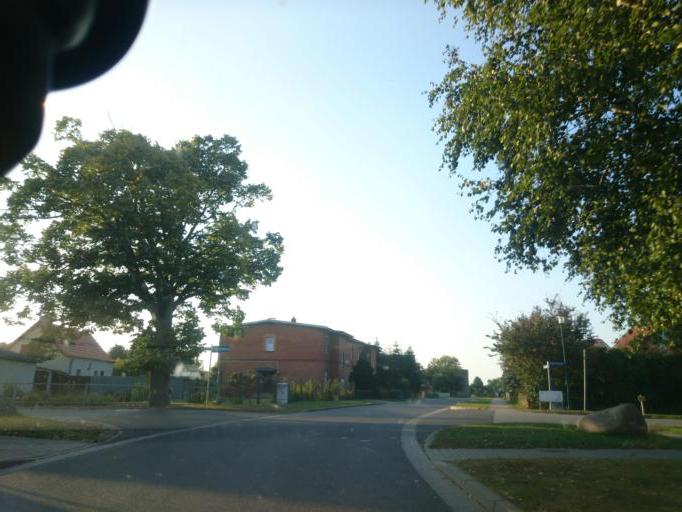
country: DE
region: Mecklenburg-Vorpommern
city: Saal
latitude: 54.3100
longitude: 12.5011
